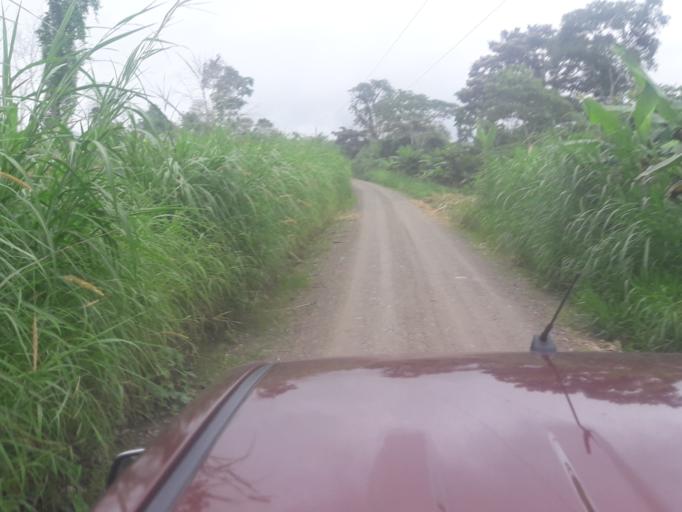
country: EC
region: Napo
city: Tena
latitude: -1.0274
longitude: -77.6060
